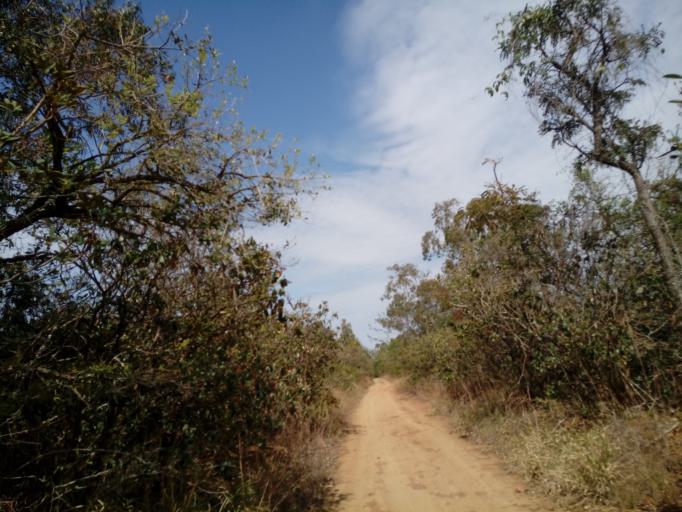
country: BR
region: Sao Paulo
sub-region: Sao Carlos
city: Sao Carlos
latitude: -21.9725
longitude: -47.8816
